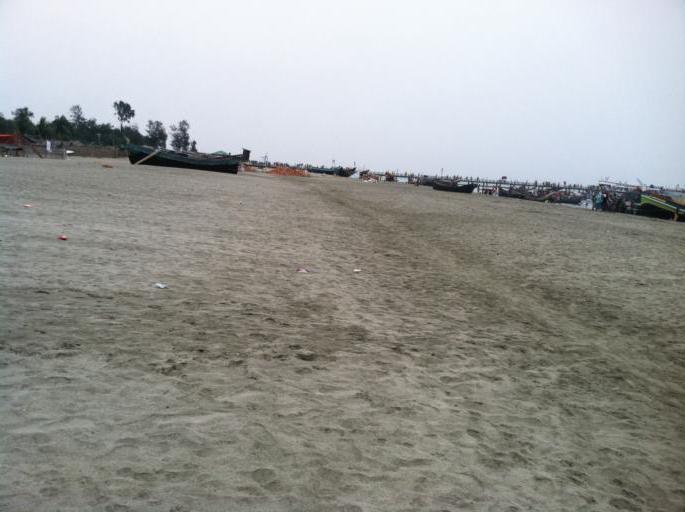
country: BD
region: Chittagong
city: Teknaf
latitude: 20.6309
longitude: 92.3271
